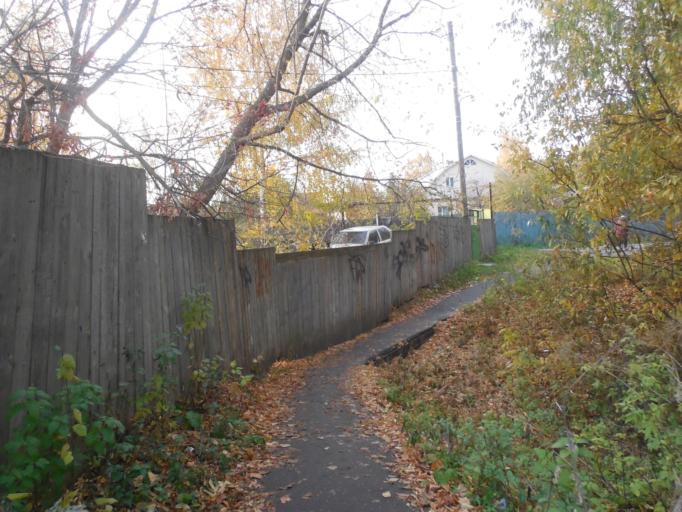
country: RU
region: Moskovskaya
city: Shcherbinka
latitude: 55.4976
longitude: 37.5850
